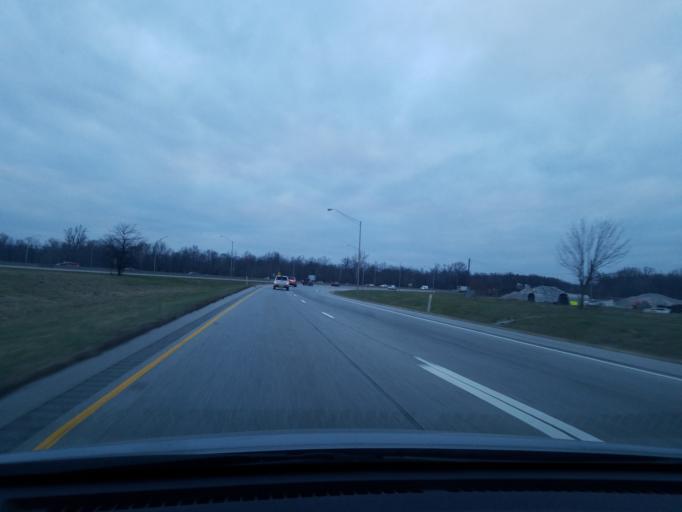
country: US
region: Indiana
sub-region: Clark County
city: Sellersburg
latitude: 38.3474
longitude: -85.7527
